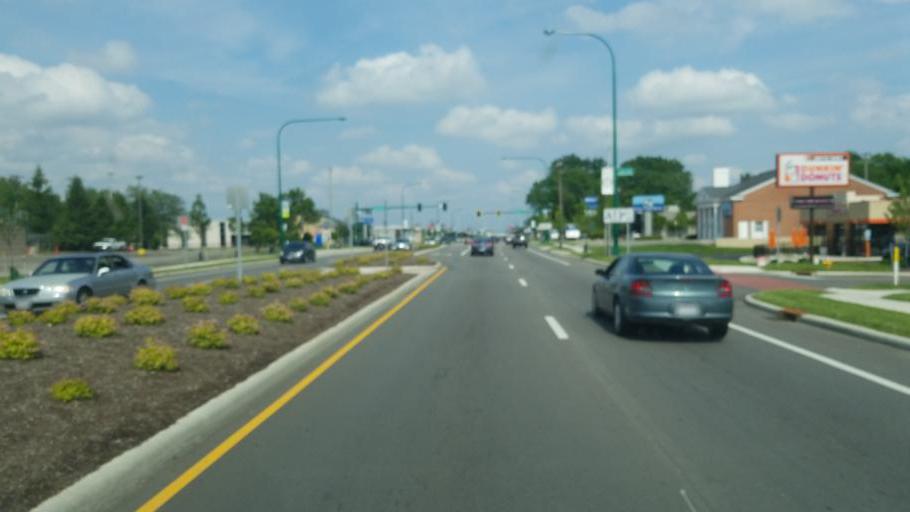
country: US
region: Ohio
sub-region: Franklin County
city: Lincoln Village
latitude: 39.9518
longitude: -83.1371
